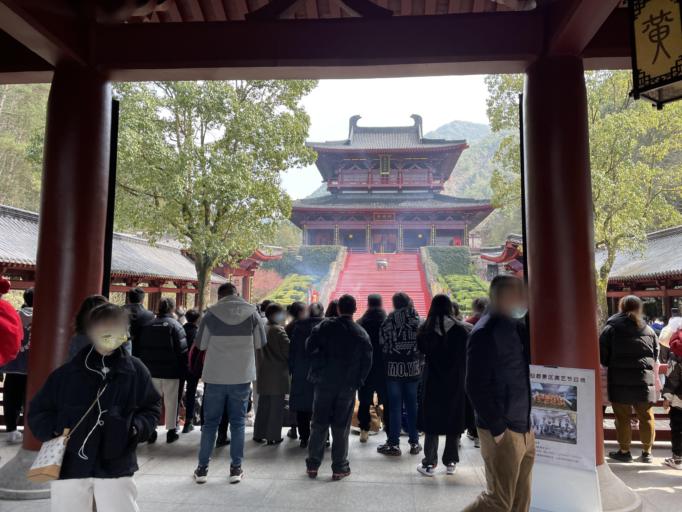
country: CN
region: Zhejiang Sheng
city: Shuhong
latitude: 28.6912
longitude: 120.1395
